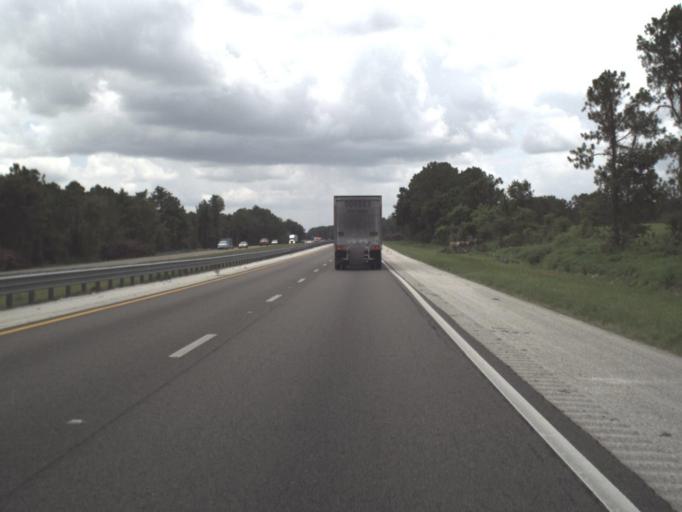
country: US
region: Florida
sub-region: Pasco County
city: Wesley Chapel
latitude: 28.2615
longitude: -82.3339
